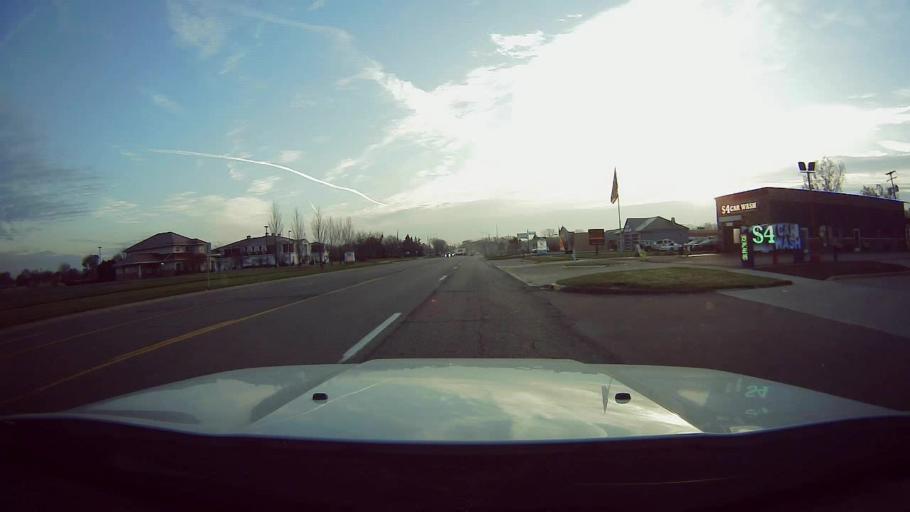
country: US
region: Michigan
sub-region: Oakland County
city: Clawson
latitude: 42.5492
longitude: -83.0915
